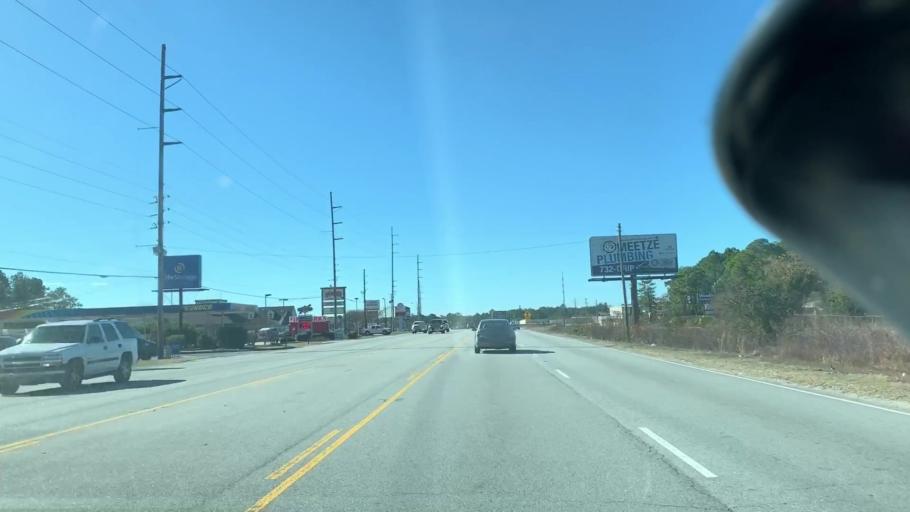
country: US
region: South Carolina
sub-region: Richland County
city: Woodfield
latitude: 34.1136
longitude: -80.8914
